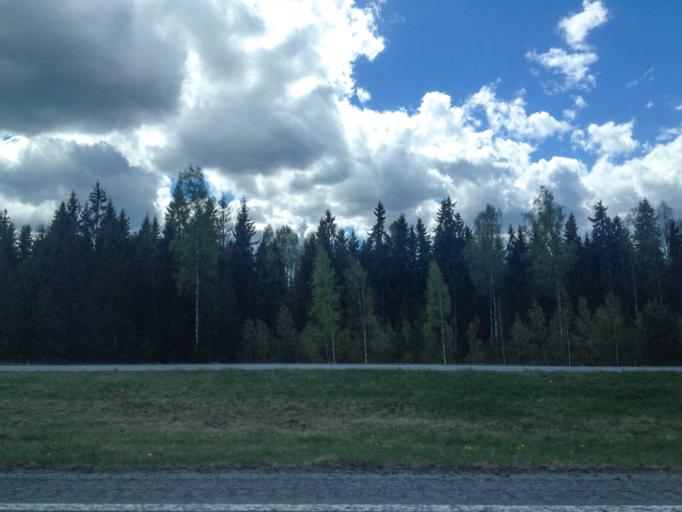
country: FI
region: Haeme
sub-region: Haemeenlinna
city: Kalvola
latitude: 61.1338
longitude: 24.0950
